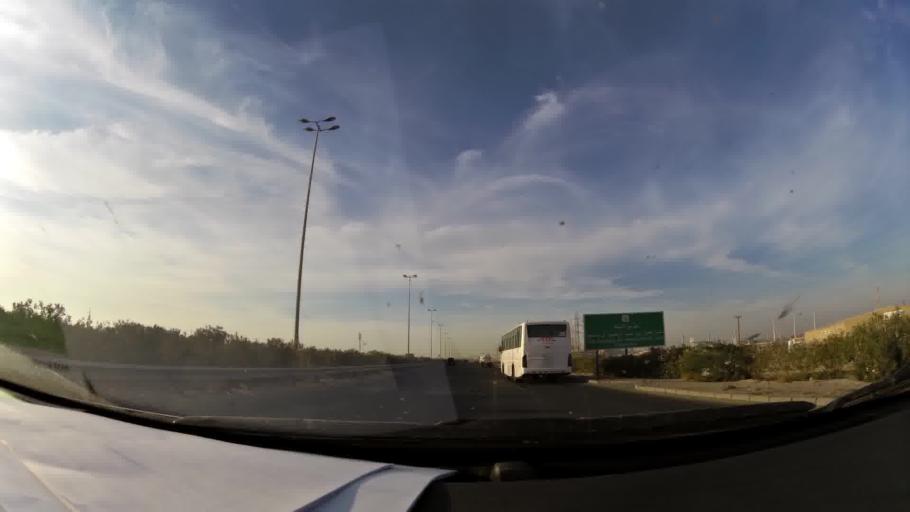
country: KW
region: Al Ahmadi
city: Al Fahahil
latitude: 28.9796
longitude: 48.1561
